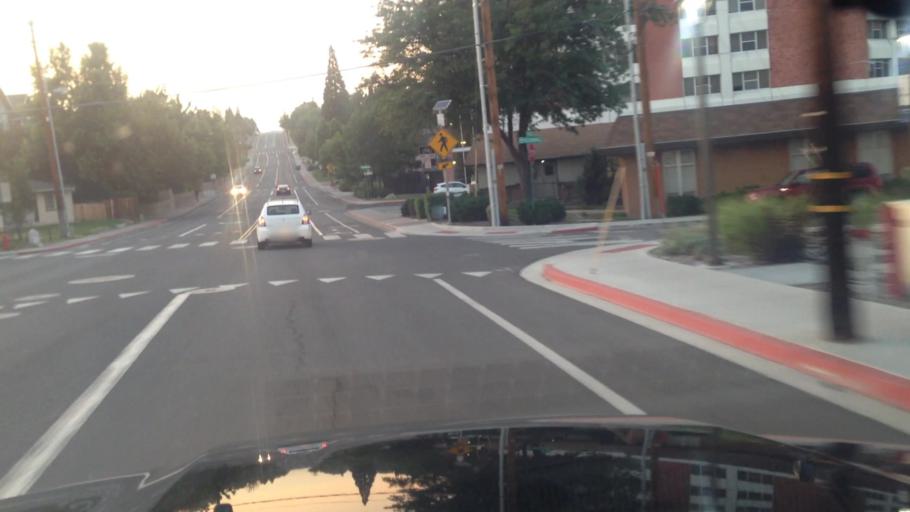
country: US
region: Nevada
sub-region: Washoe County
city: Reno
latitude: 39.5379
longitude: -119.8184
